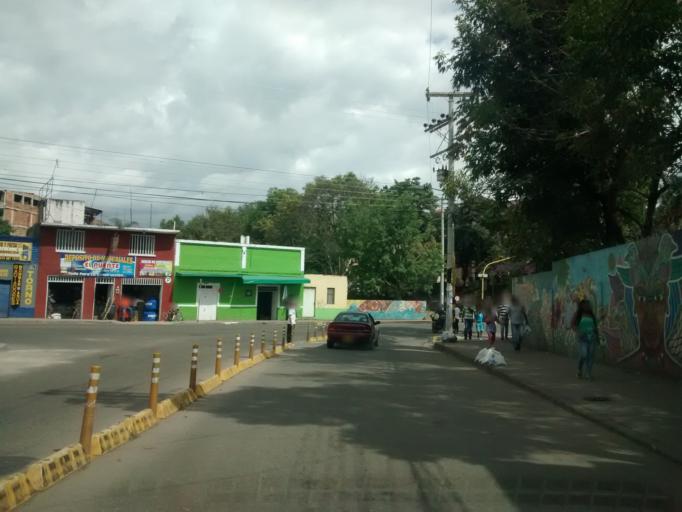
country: CO
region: Cundinamarca
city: Fusagasuga
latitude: 4.3395
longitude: -74.3637
